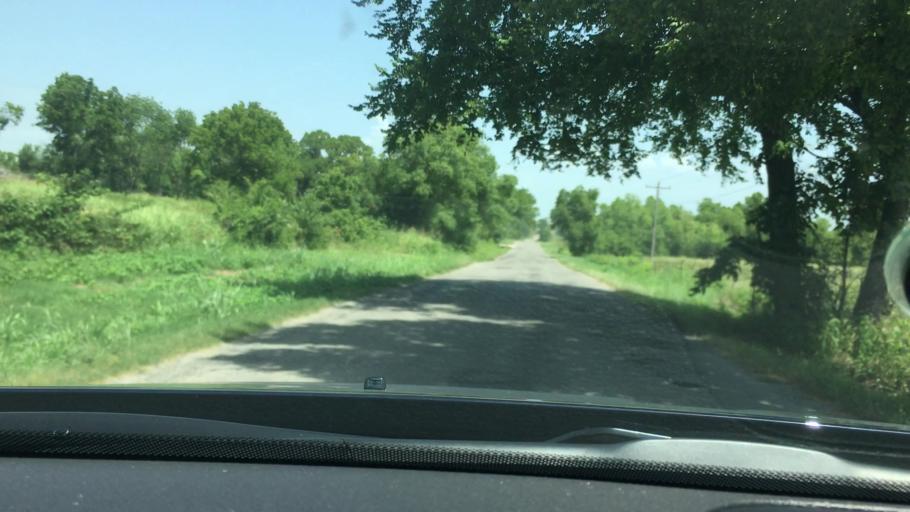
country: US
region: Oklahoma
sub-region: Pontotoc County
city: Byng
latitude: 34.8345
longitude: -96.6698
